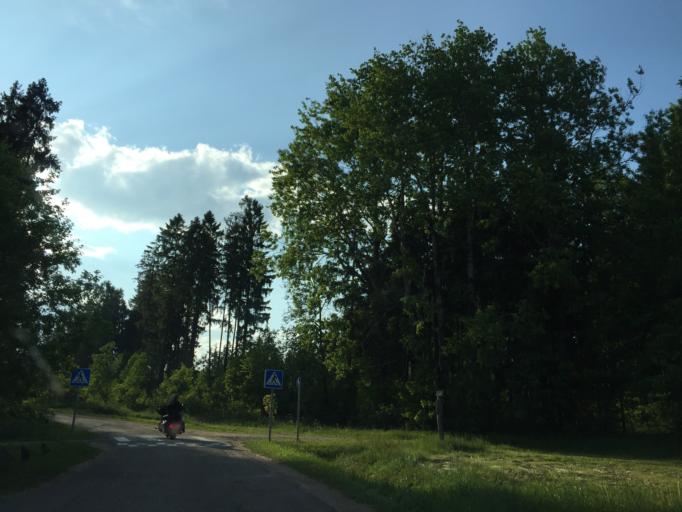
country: LT
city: Plateliai
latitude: 56.0492
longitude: 21.8313
